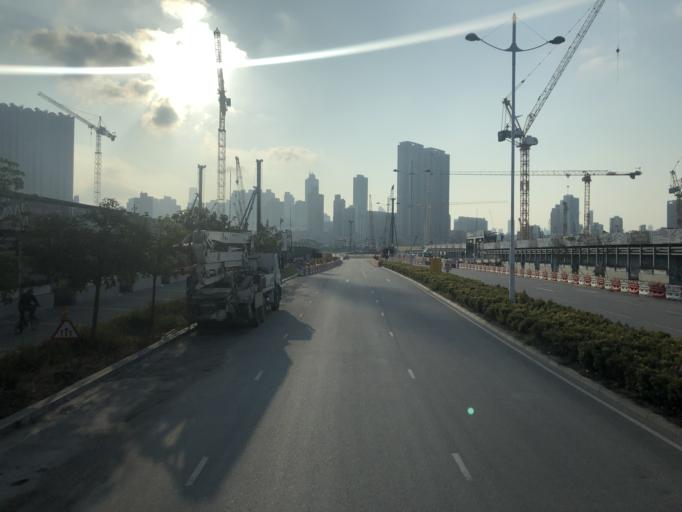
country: HK
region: Kowloon City
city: Kowloon
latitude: 22.3245
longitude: 114.1990
